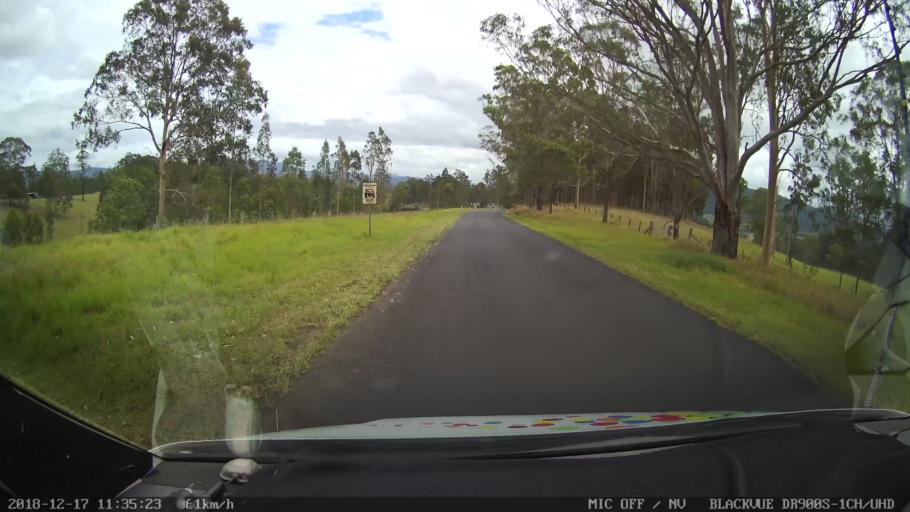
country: AU
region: New South Wales
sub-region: Kyogle
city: Kyogle
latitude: -28.7232
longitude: 152.6067
